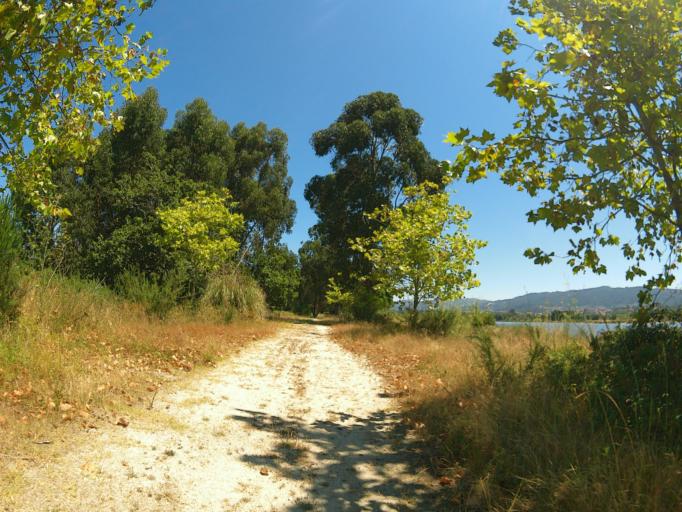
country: PT
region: Viana do Castelo
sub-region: Viana do Castelo
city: Darque
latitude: 41.7028
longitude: -8.7409
